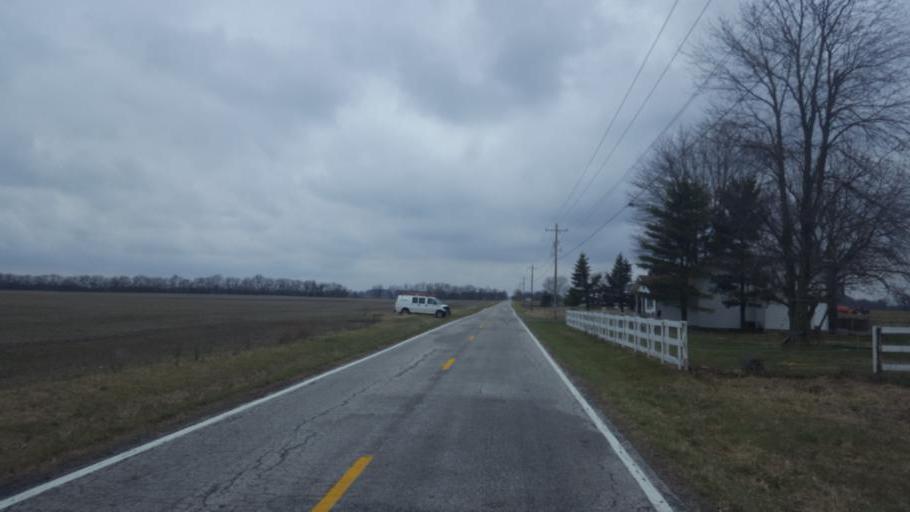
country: US
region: Ohio
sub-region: Delaware County
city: Ashley
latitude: 40.3956
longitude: -82.9677
